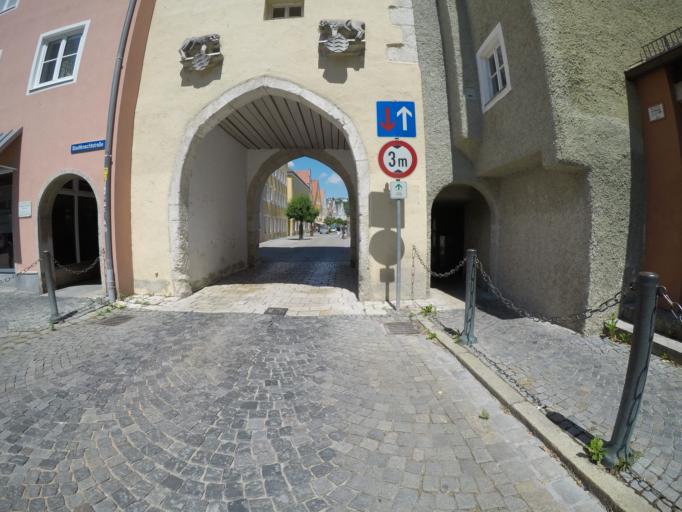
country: DE
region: Bavaria
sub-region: Lower Bavaria
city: Kelheim
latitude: 48.9166
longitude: 11.8711
